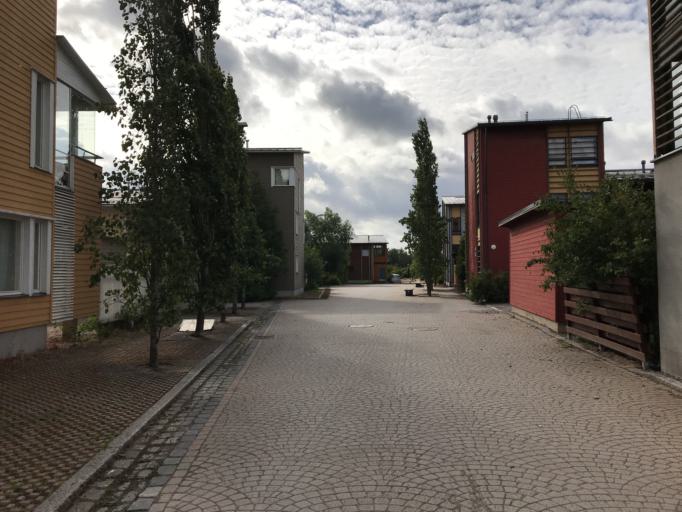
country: FI
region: Uusimaa
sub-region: Helsinki
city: Vantaa
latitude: 60.2262
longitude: 25.0303
